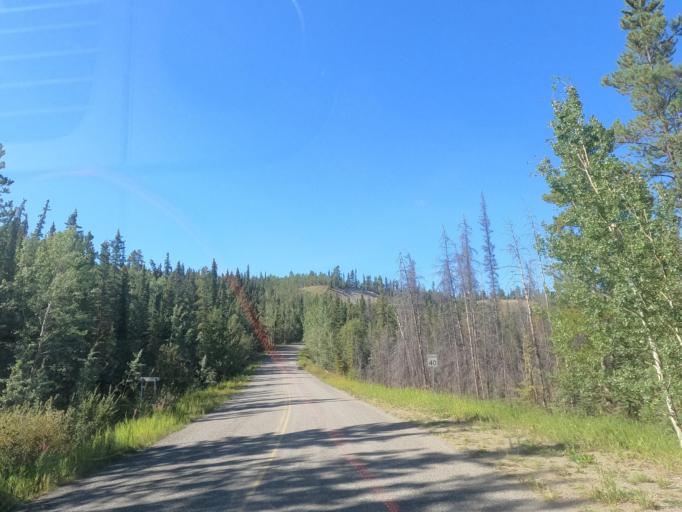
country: CA
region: Yukon
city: Whitehorse
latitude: 60.6642
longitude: -135.0340
